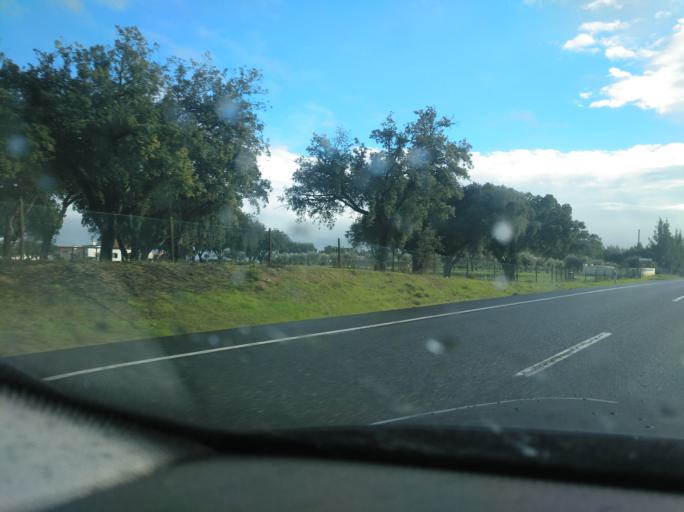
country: PT
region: Setubal
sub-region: Grandola
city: Grandola
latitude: 38.0382
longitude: -8.4009
